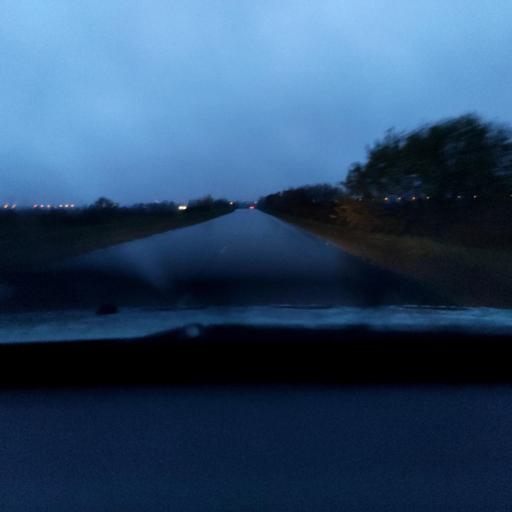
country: RU
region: Perm
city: Kondratovo
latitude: 57.9931
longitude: 56.0904
